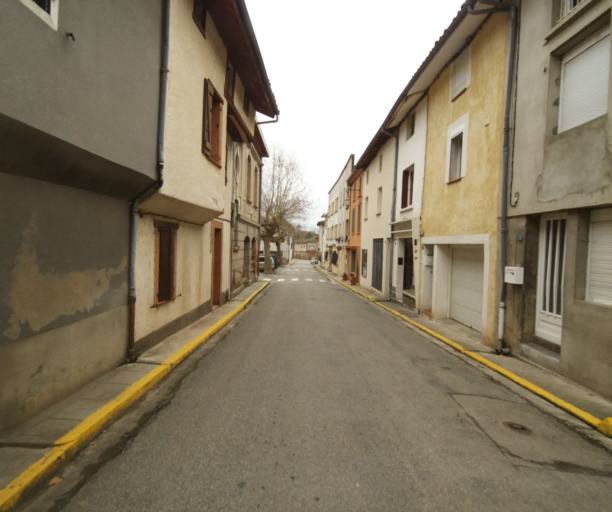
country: FR
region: Midi-Pyrenees
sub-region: Departement de l'Ariege
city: Pamiers
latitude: 43.1656
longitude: 1.5916
